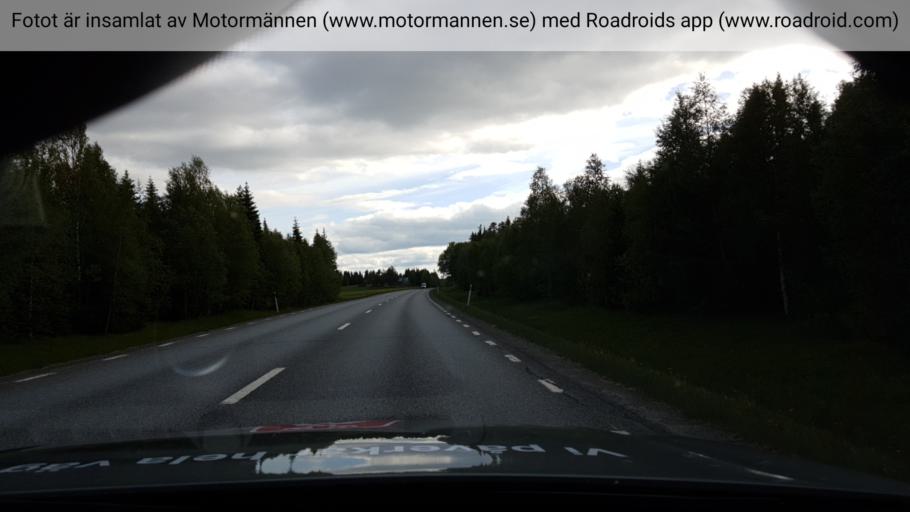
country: SE
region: Jaemtland
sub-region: OEstersunds Kommun
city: Lit
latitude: 63.4277
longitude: 15.1175
